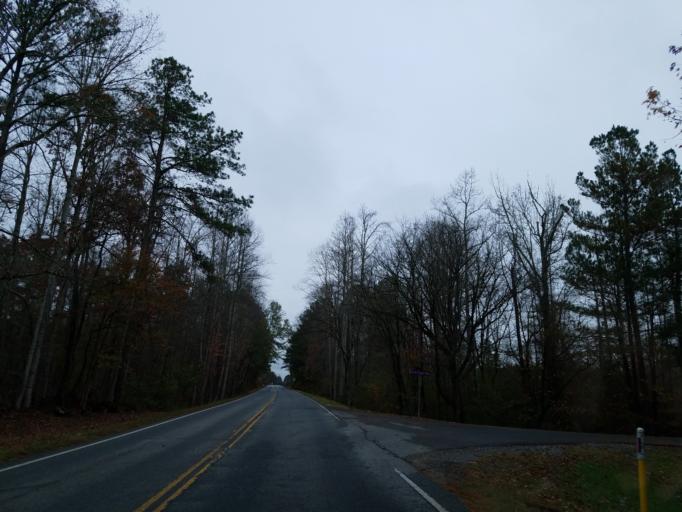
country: US
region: Georgia
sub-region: Cherokee County
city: Canton
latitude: 34.3228
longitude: -84.5455
